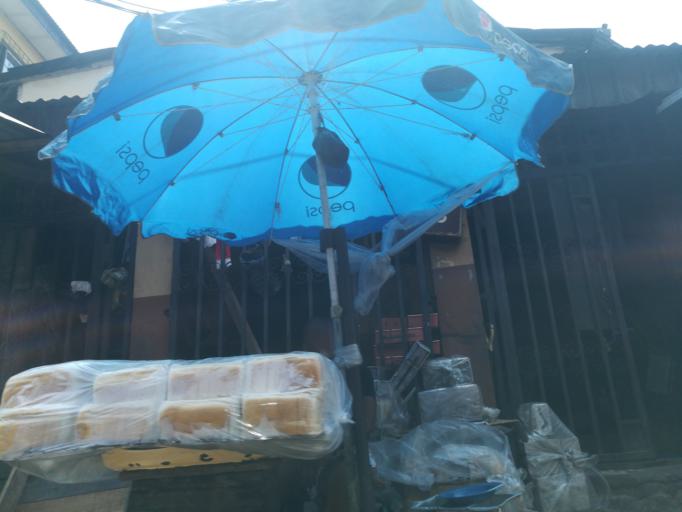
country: NG
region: Lagos
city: Lagos
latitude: 6.4535
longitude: 3.3947
